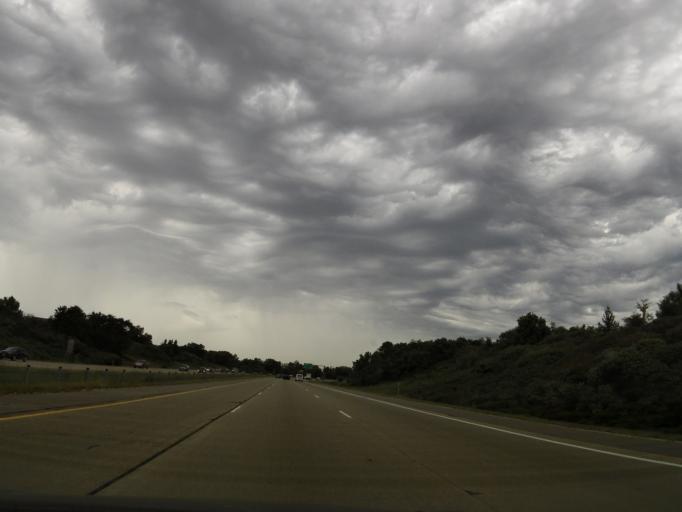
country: US
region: Minnesota
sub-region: Dakota County
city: Eagan
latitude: 44.8193
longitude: -93.1726
